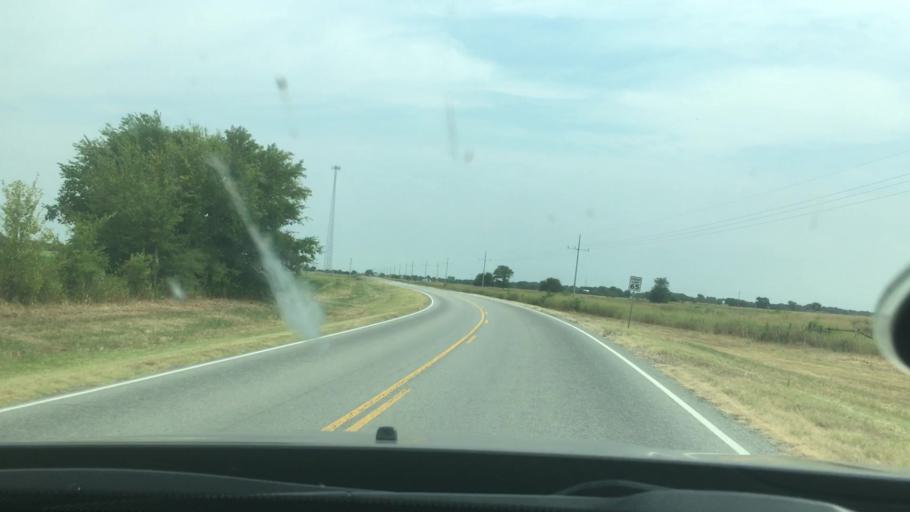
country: US
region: Oklahoma
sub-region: Coal County
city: Coalgate
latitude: 34.5013
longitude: -96.4071
